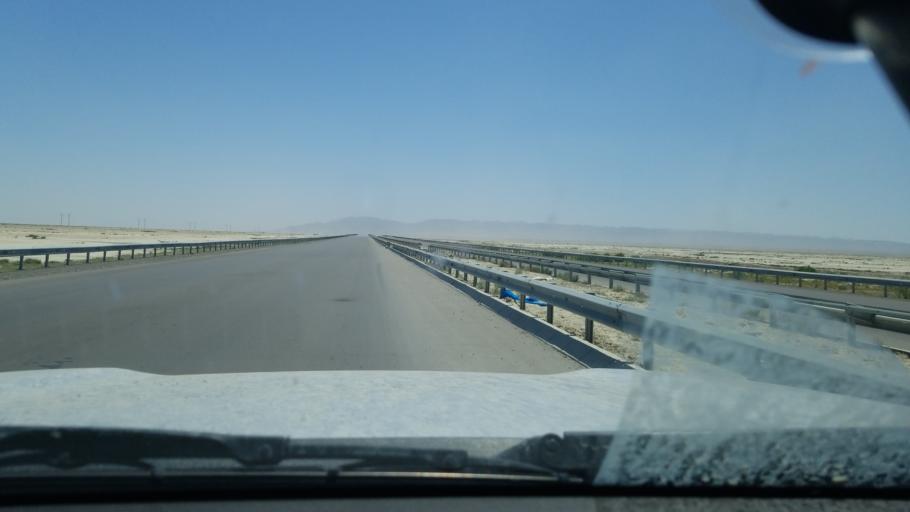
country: TM
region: Balkan
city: Gazanjyk
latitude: 39.2816
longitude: 55.2440
